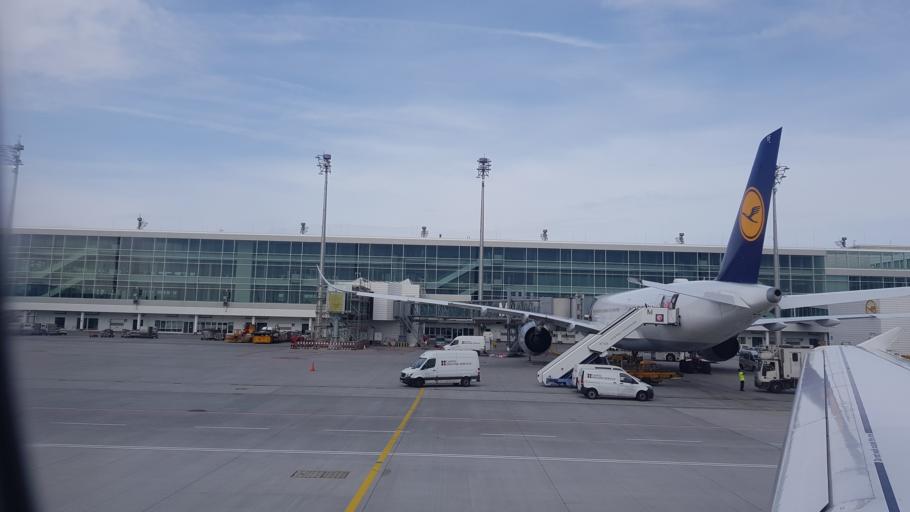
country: DE
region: Bavaria
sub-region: Upper Bavaria
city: Hallbergmoos
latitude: 48.3529
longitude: 11.8005
